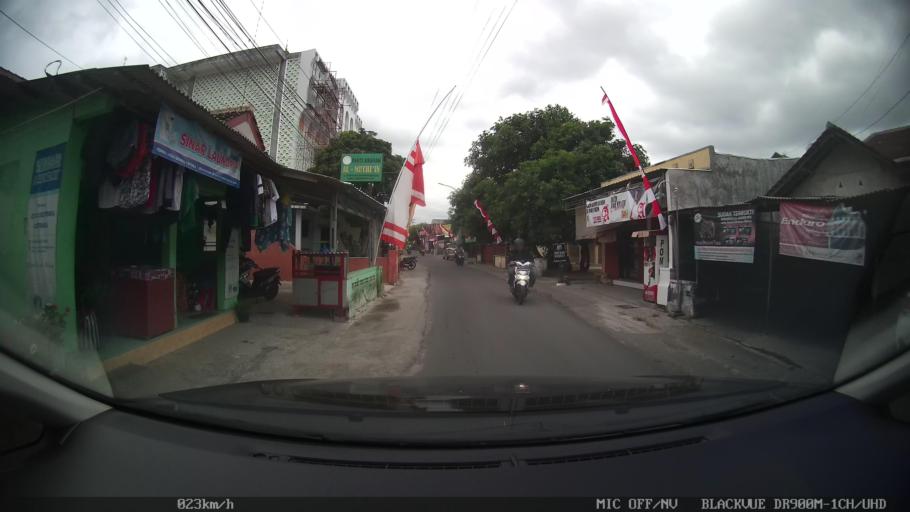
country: ID
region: Daerah Istimewa Yogyakarta
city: Depok
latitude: -7.8044
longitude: 110.4160
